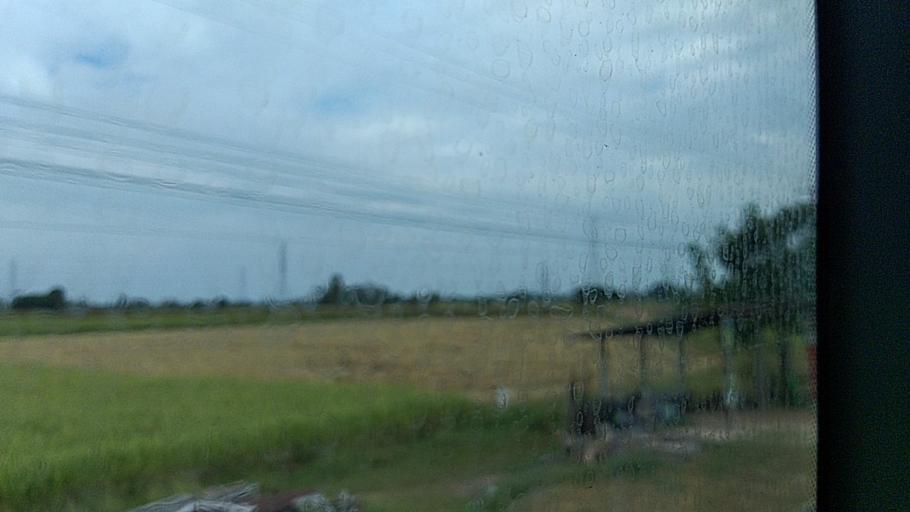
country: TH
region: Roi Et
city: Si Somdet
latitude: 16.1262
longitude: 103.4734
